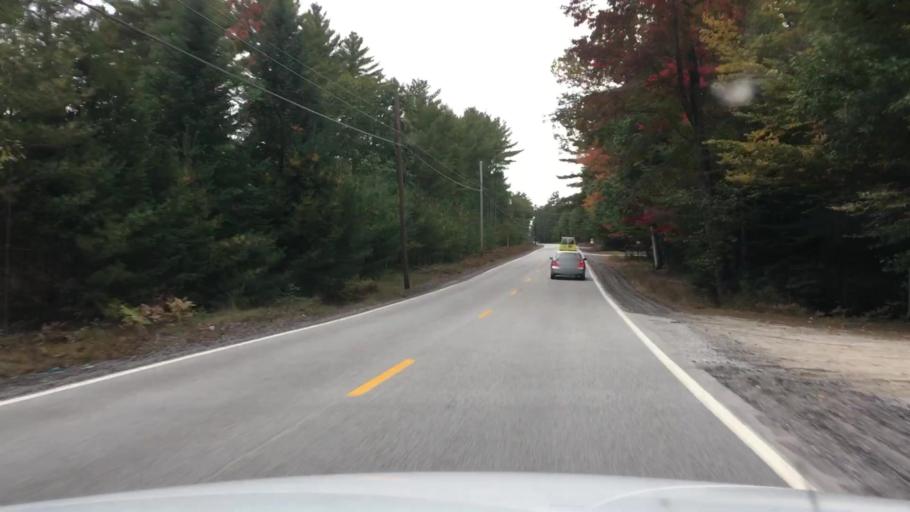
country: US
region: Maine
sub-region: Cumberland County
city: Harrison
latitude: 44.2168
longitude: -70.6864
